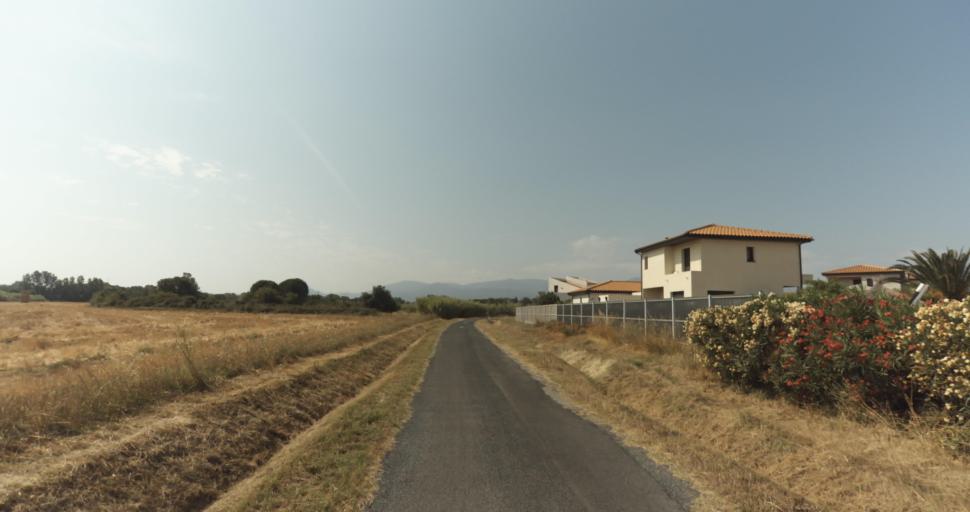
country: FR
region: Languedoc-Roussillon
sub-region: Departement des Pyrenees-Orientales
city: Latour-Bas-Elne
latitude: 42.6152
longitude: 3.0167
